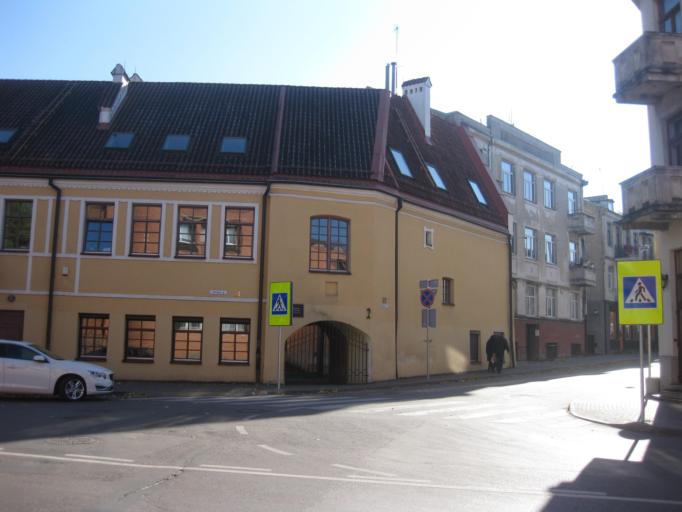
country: LT
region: Kauno apskritis
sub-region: Kaunas
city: Kaunas
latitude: 54.9001
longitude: 23.8912
